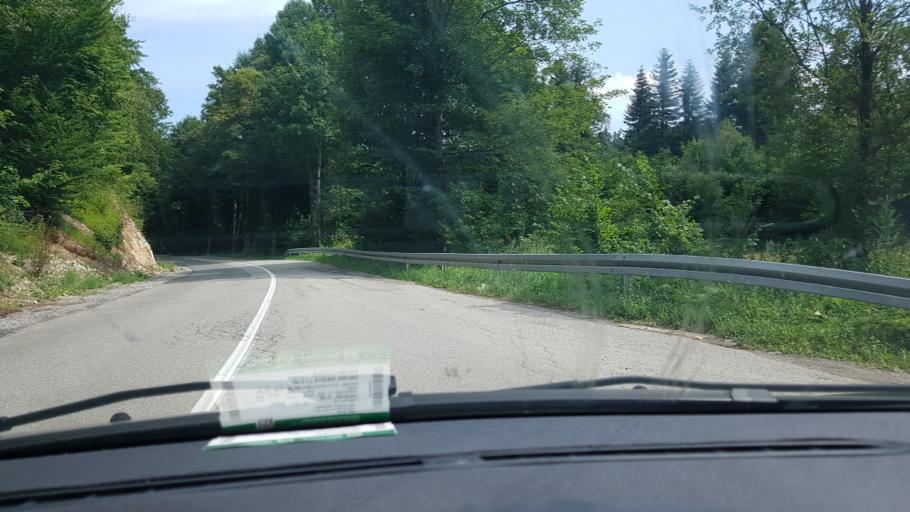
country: HR
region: Primorsko-Goranska
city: Hreljin
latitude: 45.3309
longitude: 14.6924
